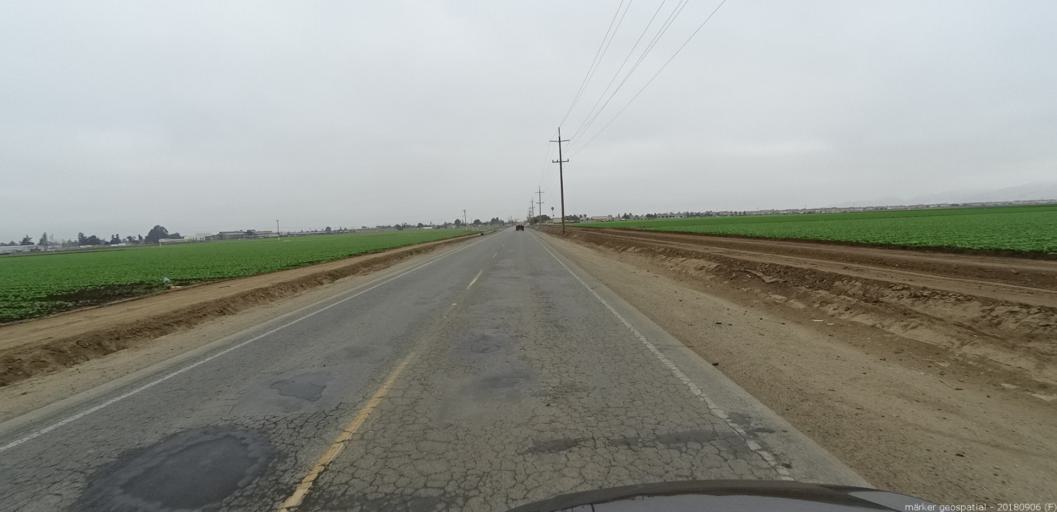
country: US
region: California
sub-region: Monterey County
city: Salinas
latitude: 36.6671
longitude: -121.5960
